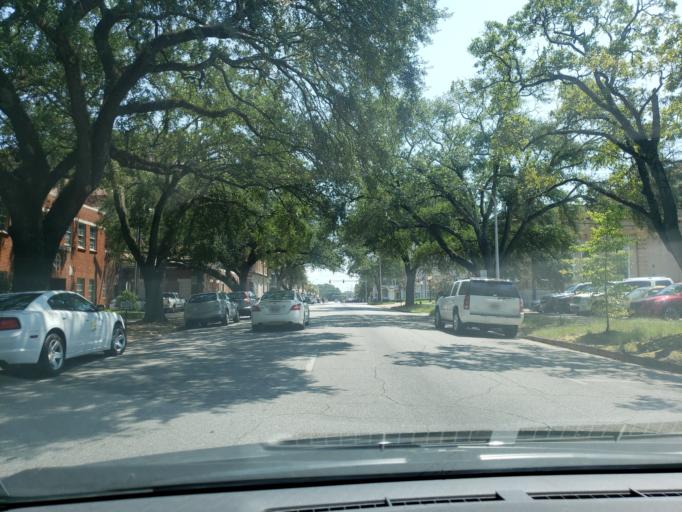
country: US
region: Georgia
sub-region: Dougherty County
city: Albany
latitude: 31.5796
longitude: -84.1537
